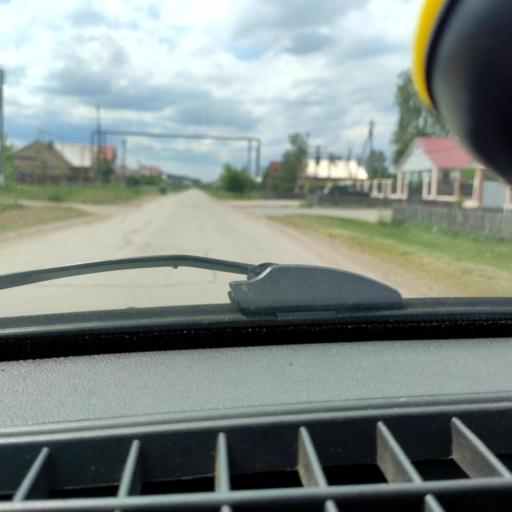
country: RU
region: Samara
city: Povolzhskiy
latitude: 53.6400
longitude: 49.6830
